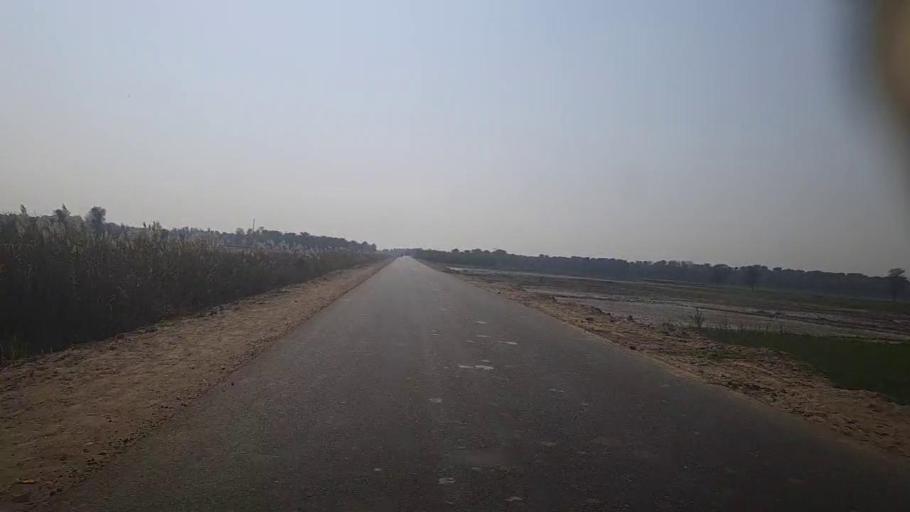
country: PK
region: Sindh
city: Khairpur
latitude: 27.4712
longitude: 68.8213
